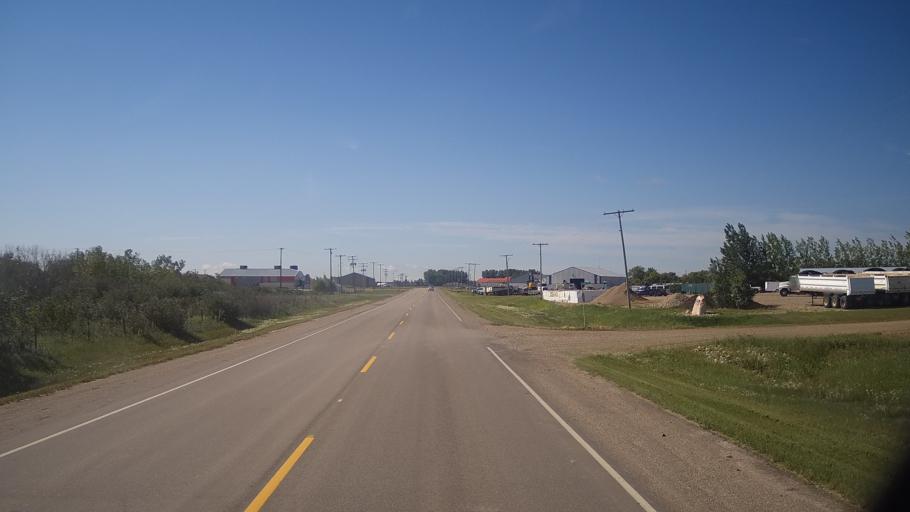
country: CA
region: Saskatchewan
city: Watrous
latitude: 51.6724
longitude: -105.4518
